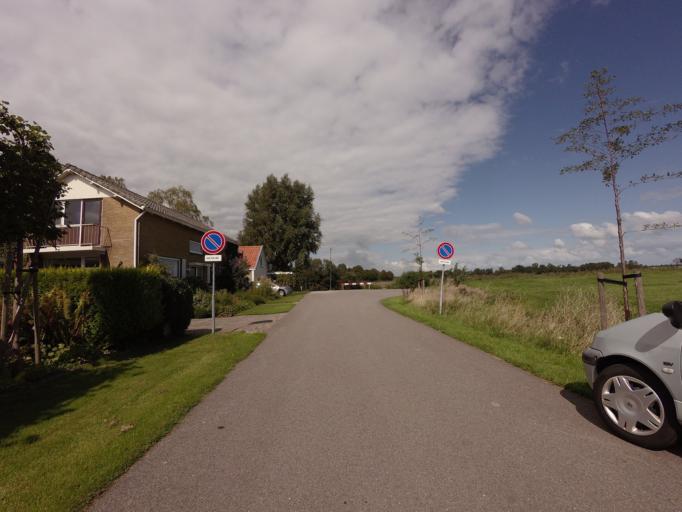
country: NL
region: Friesland
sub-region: Sudwest Fryslan
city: IJlst
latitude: 52.9998
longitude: 5.6475
